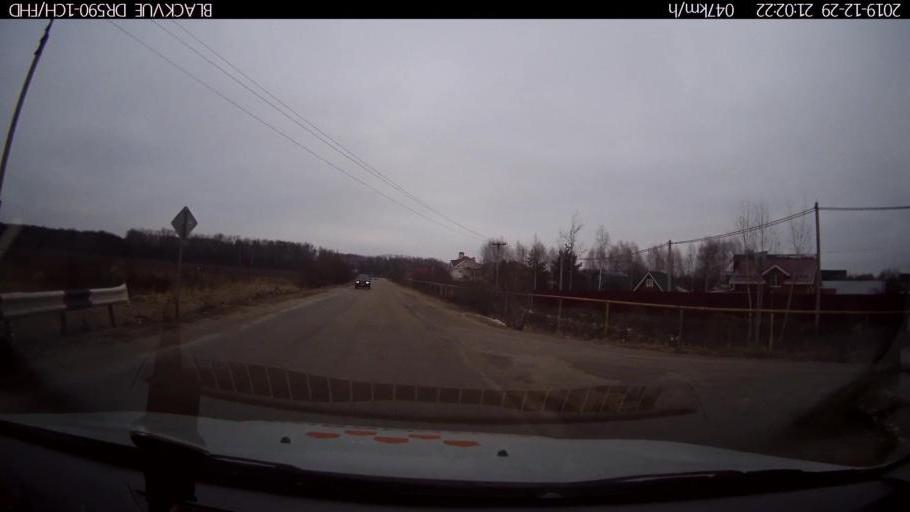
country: RU
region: Nizjnij Novgorod
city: Afonino
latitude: 56.1904
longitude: 44.0002
